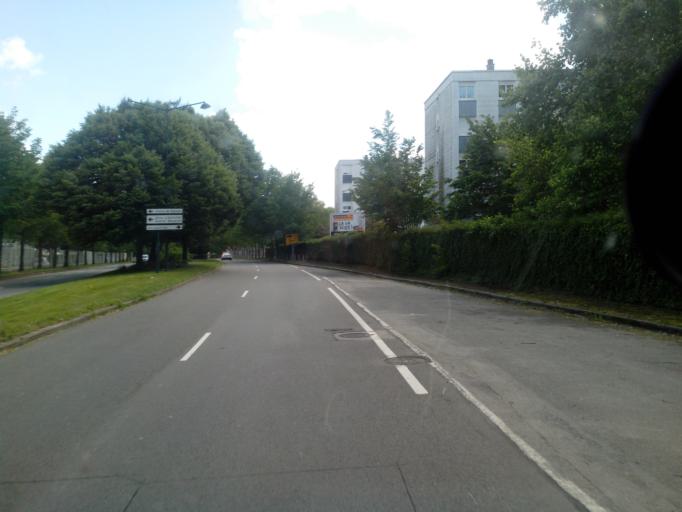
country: FR
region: Brittany
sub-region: Departement d'Ille-et-Vilaine
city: Montgermont
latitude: 48.1242
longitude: -1.7126
